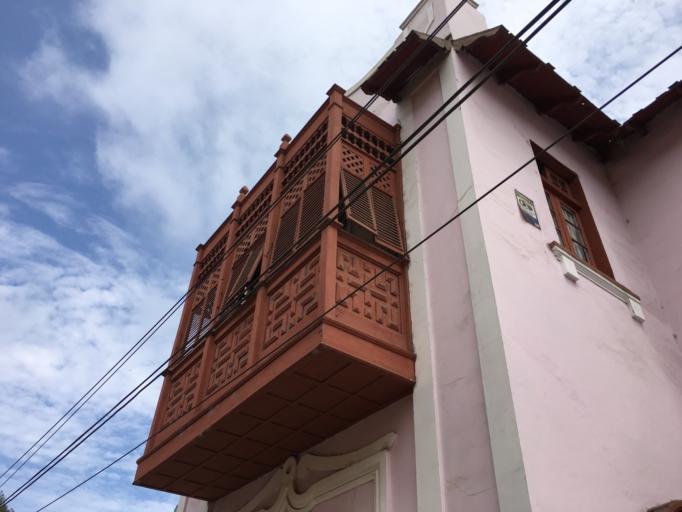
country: PE
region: Lima
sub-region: Lima
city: Surco
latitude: -12.1501
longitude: -77.0225
